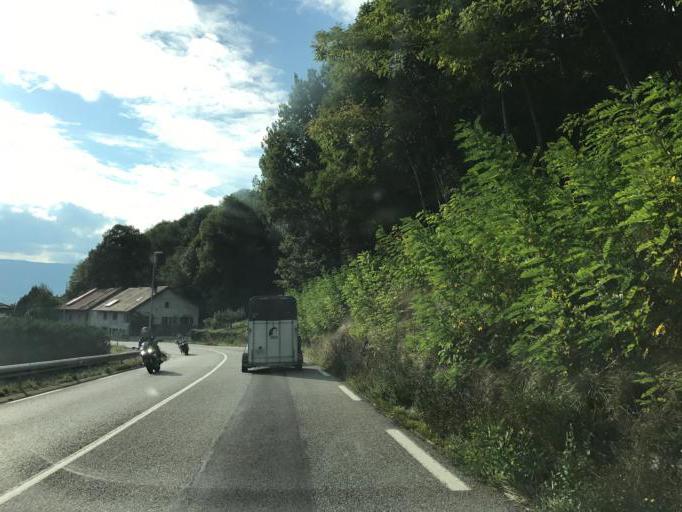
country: FR
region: Rhone-Alpes
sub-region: Departement de l'Ain
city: Bellegarde-sur-Valserine
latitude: 46.0922
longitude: 5.8671
